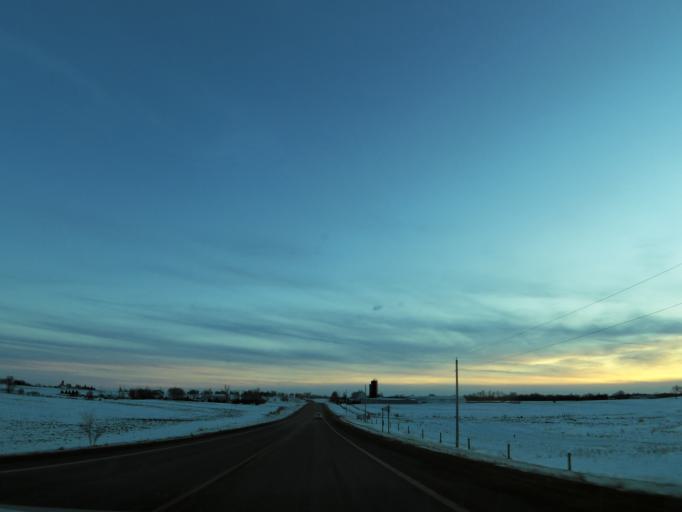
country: US
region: Minnesota
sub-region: Carver County
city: Chaska
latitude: 44.7466
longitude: -93.5617
